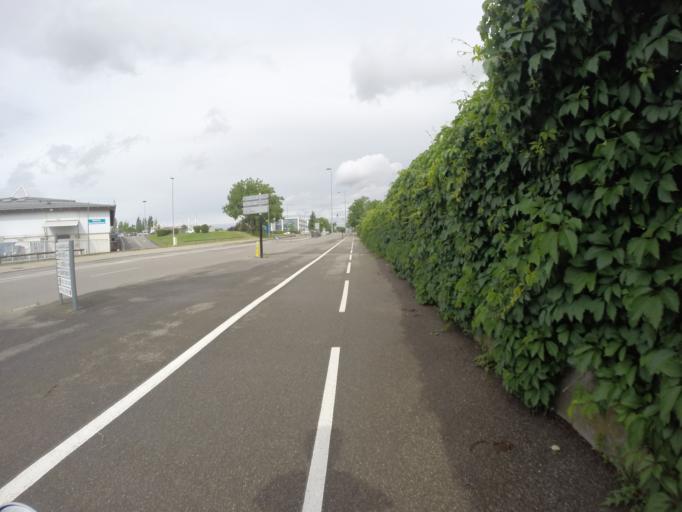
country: FR
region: Rhone-Alpes
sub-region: Departement du Rhone
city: Bron
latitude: 45.7267
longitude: 4.9296
